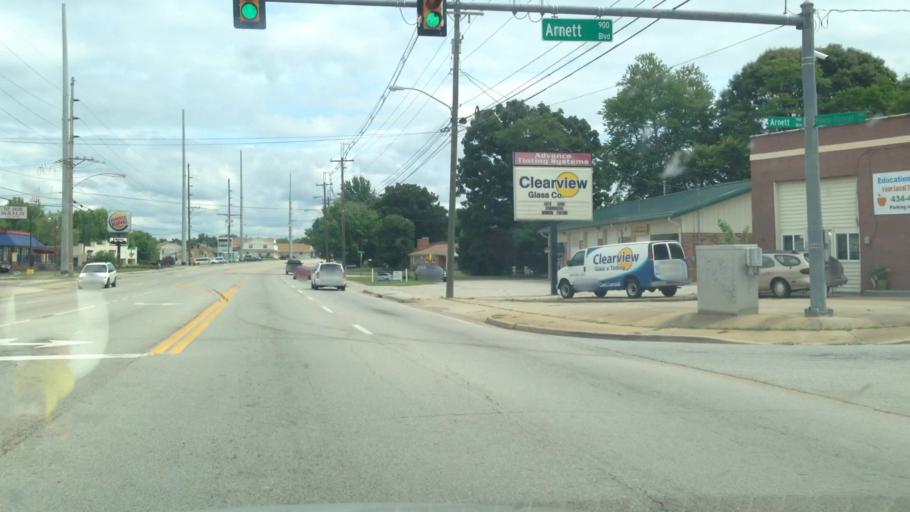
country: US
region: Virginia
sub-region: City of Danville
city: Danville
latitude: 36.6237
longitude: -79.4038
